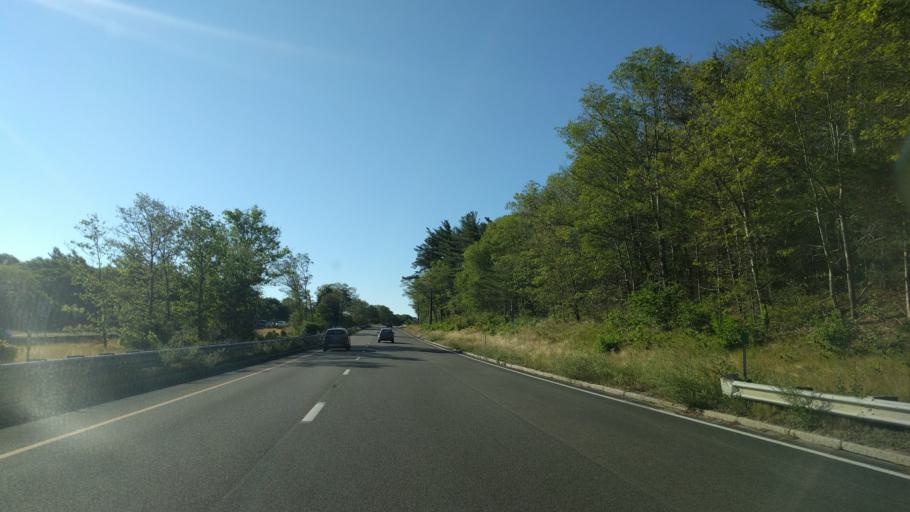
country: US
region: Massachusetts
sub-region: Barnstable County
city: East Sandwich
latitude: 41.7167
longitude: -70.4206
